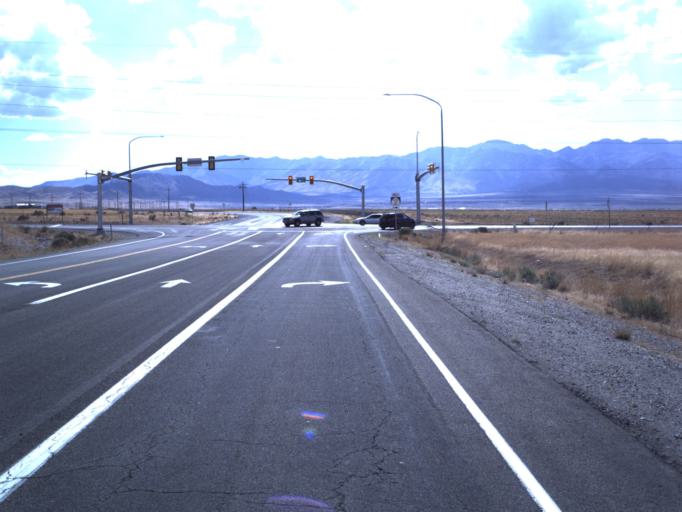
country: US
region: Utah
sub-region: Tooele County
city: Tooele
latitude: 40.5488
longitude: -112.3410
